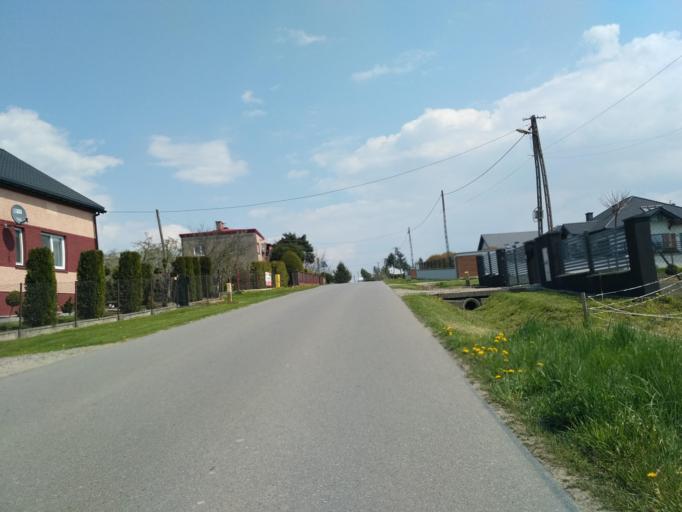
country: PL
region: Subcarpathian Voivodeship
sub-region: Powiat jasielski
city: Tarnowiec
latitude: 49.7450
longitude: 21.5495
